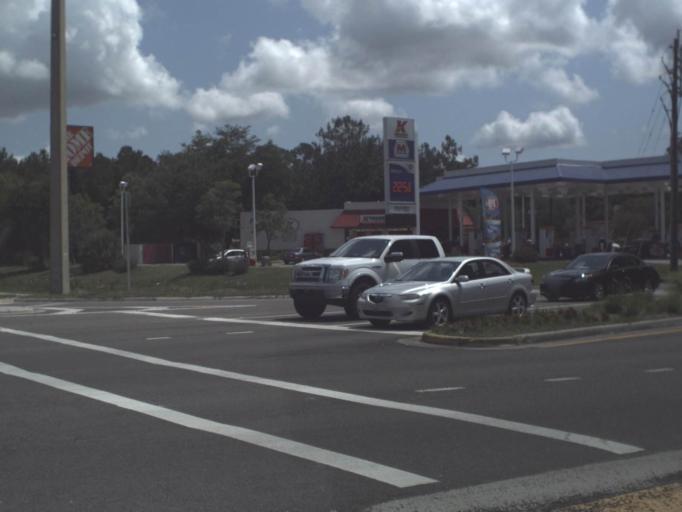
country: US
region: Florida
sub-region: Saint Johns County
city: Fruit Cove
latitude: 30.1951
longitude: -81.5516
